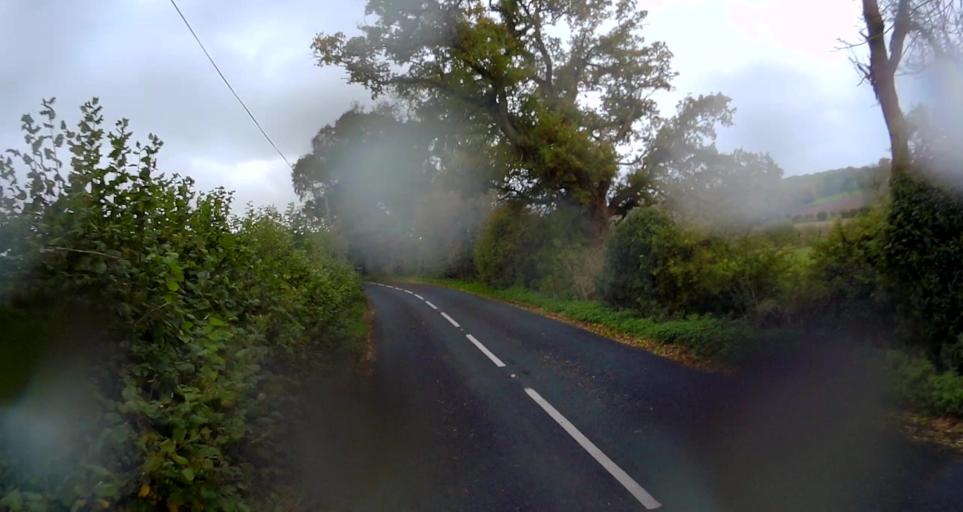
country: GB
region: England
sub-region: Hampshire
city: Kings Worthy
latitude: 51.1369
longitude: -1.1861
